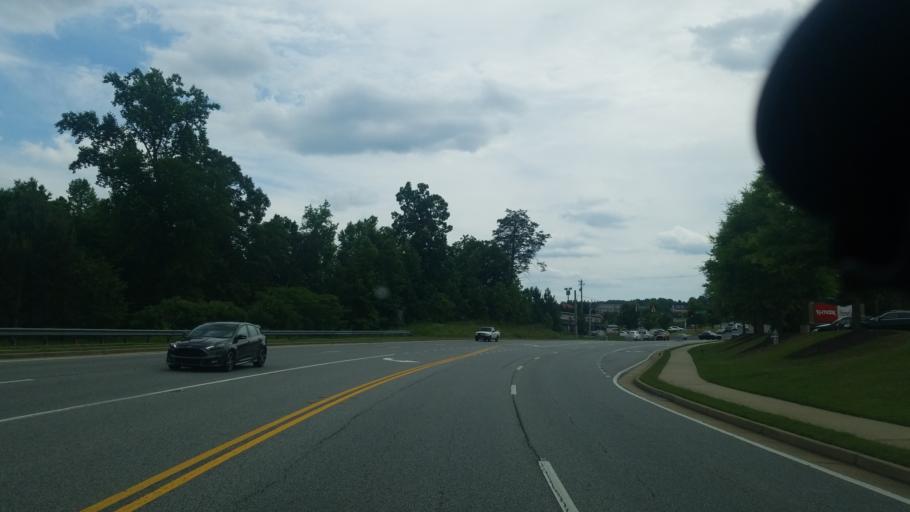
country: US
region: Georgia
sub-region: Forsyth County
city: Cumming
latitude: 34.1912
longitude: -84.1288
